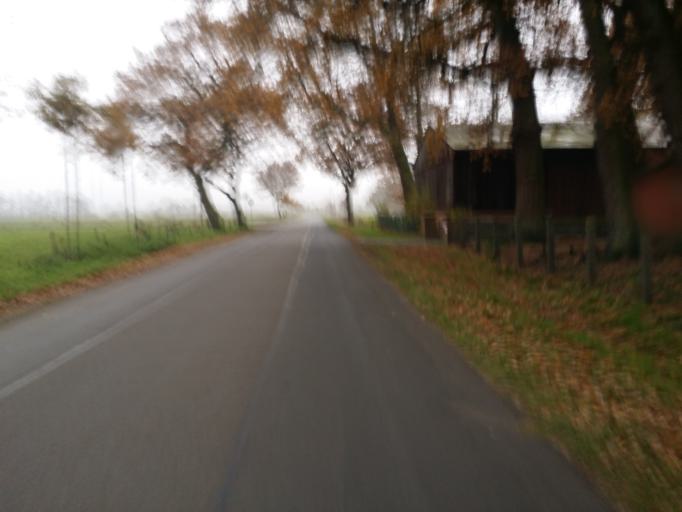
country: DE
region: Lower Saxony
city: Delmenhorst
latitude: 53.0186
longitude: 8.6230
